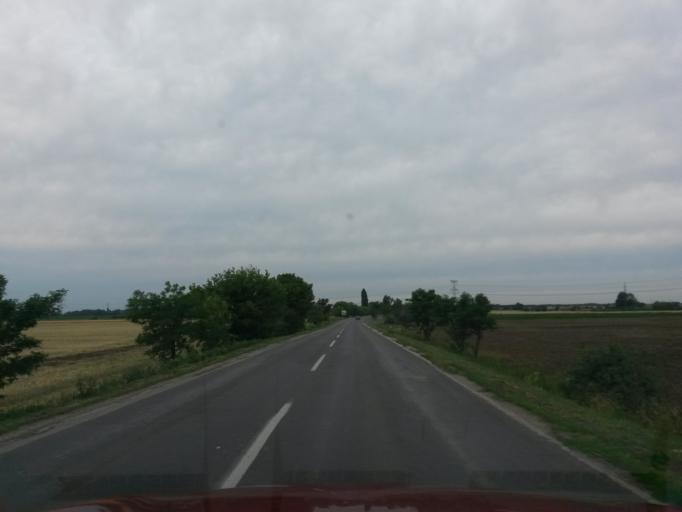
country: SK
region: Nitriansky
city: Surany
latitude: 48.0943
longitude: 18.2524
